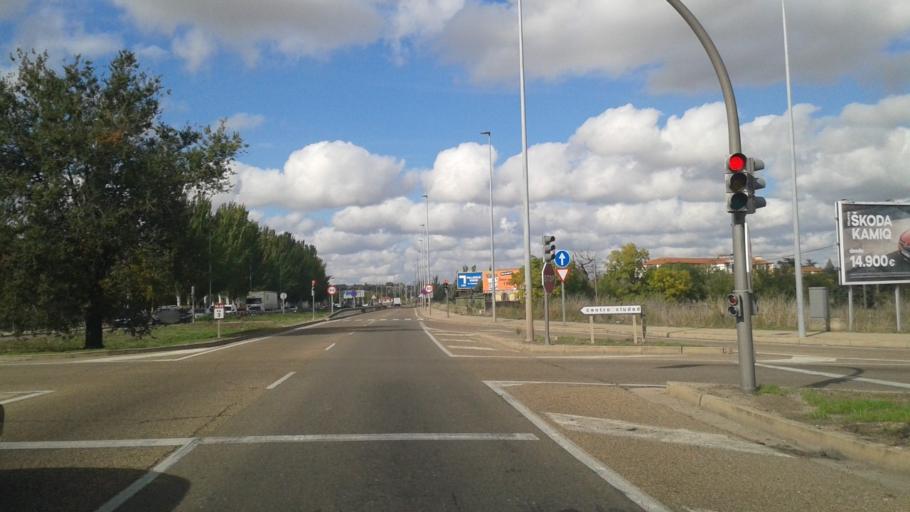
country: ES
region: Castille and Leon
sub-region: Provincia de Valladolid
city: Valladolid
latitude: 41.6665
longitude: -4.7035
